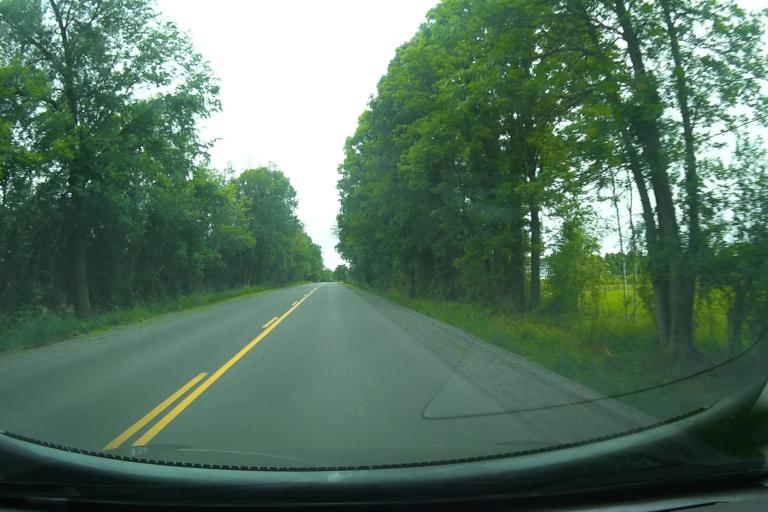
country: CA
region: Ontario
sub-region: Lanark County
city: Smiths Falls
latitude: 44.9799
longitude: -75.7892
